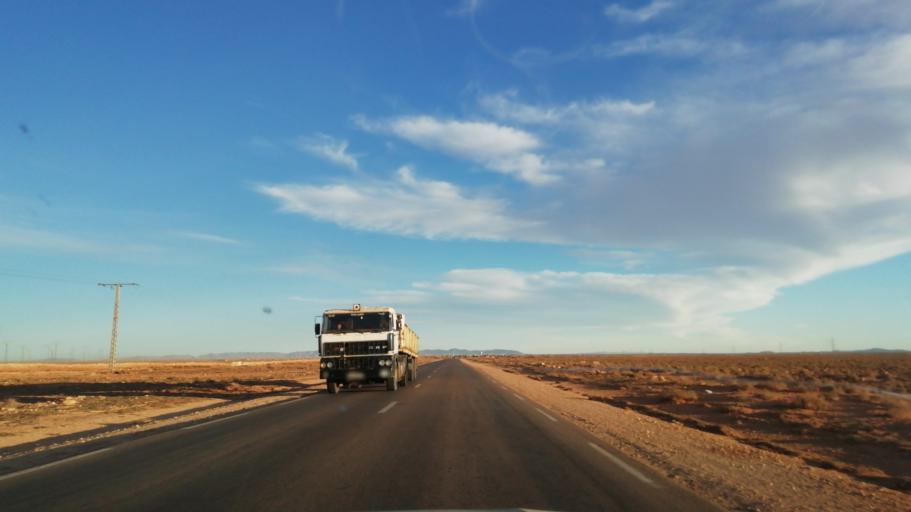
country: DZ
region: Wilaya de Naama
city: Naama
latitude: 33.7352
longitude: -0.7616
